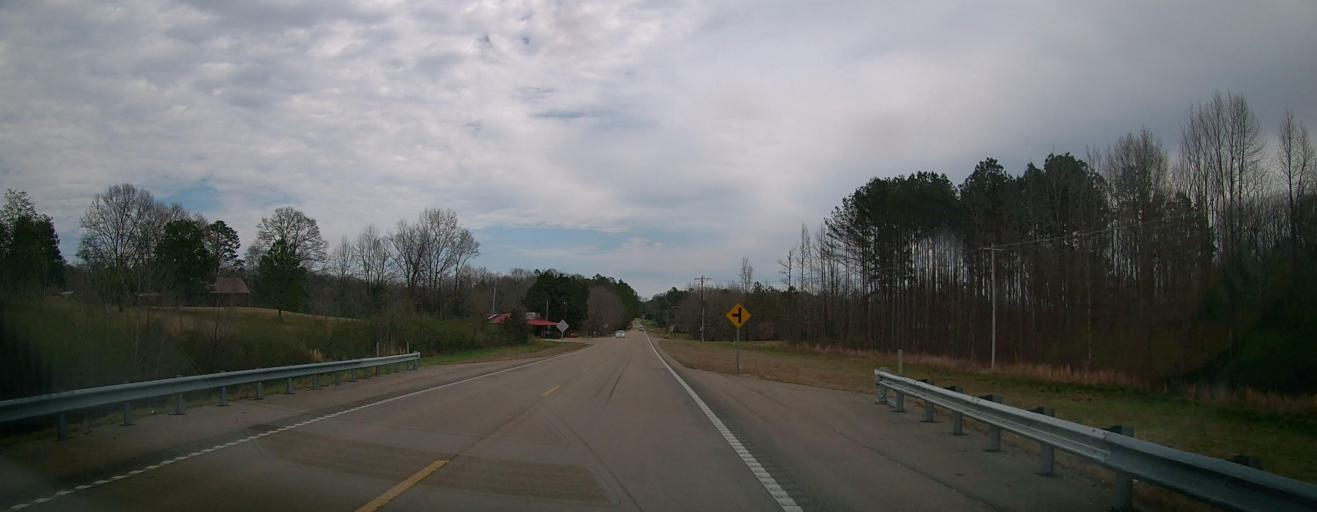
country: US
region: Mississippi
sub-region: Itawamba County
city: Fulton
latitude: 34.2526
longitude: -88.3064
